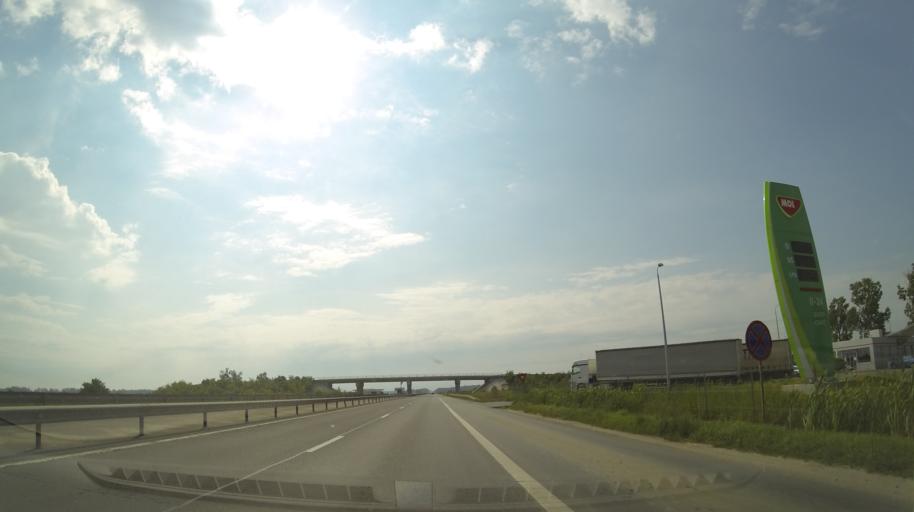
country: RO
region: Dambovita
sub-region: Comuna Corbii Mari
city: Corbii Mari
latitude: 44.5346
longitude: 25.5278
